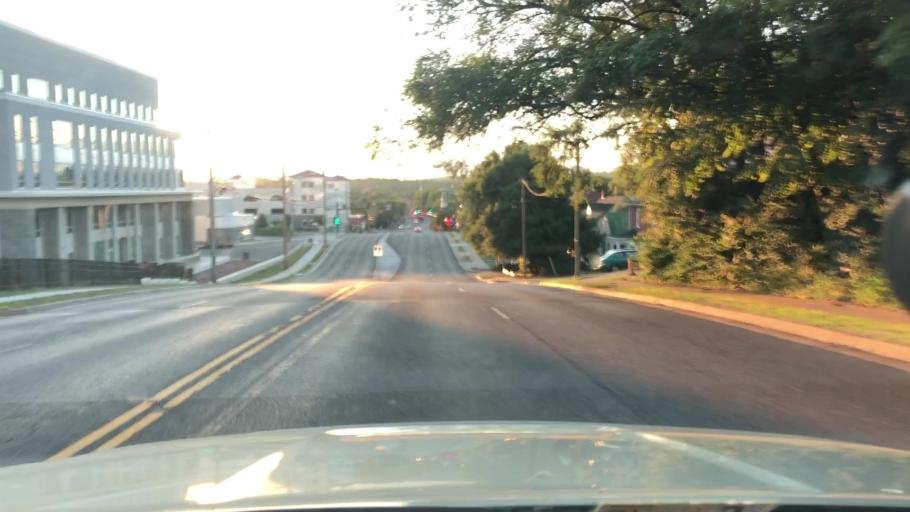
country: US
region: Virginia
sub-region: City of Harrisonburg
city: Harrisonburg
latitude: 38.4400
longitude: -78.8691
